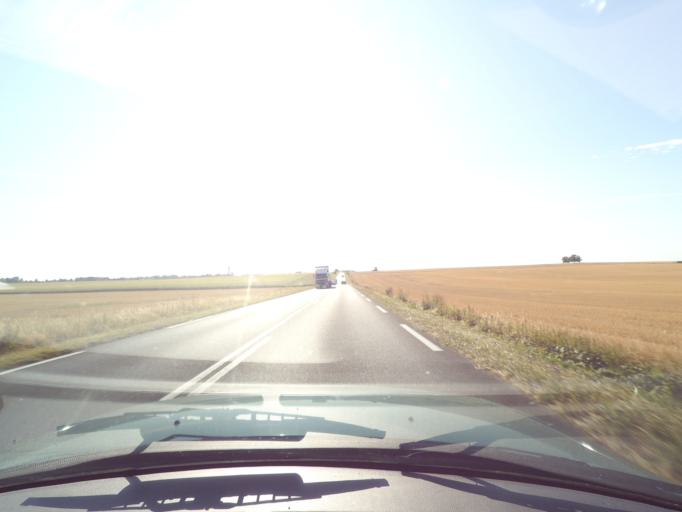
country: FR
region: Poitou-Charentes
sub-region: Departement de la Vienne
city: Cisse
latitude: 46.6348
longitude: 0.2273
